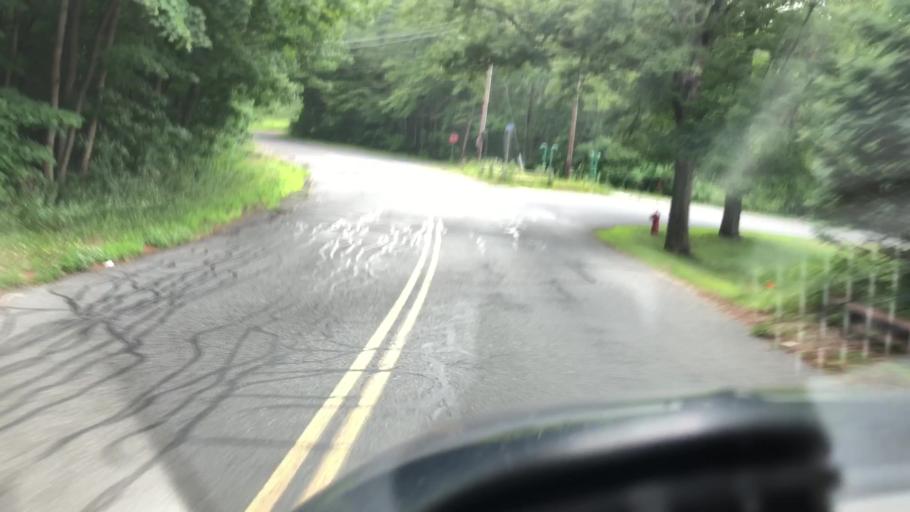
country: US
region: Massachusetts
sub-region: Hampden County
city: Holyoke
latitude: 42.1911
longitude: -72.6740
